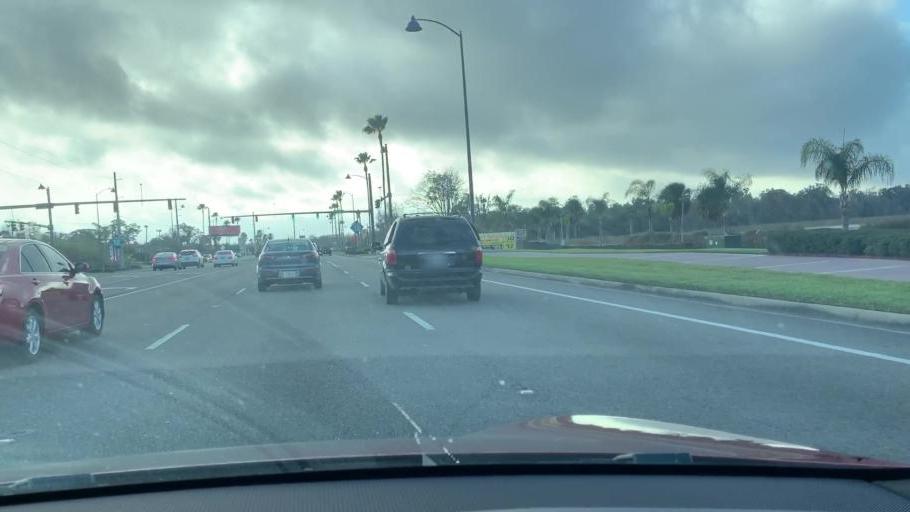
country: US
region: Florida
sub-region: Orange County
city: Hunters Creek
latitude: 28.3307
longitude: -81.4737
